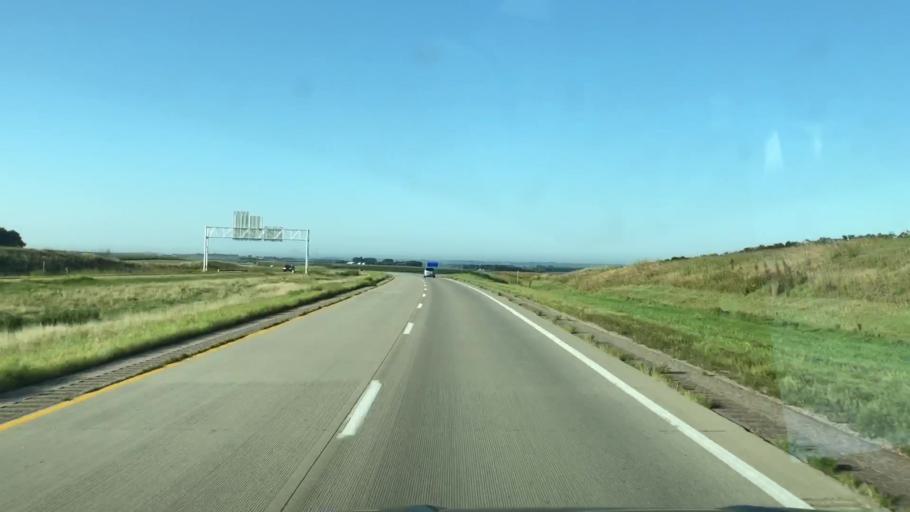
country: US
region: Iowa
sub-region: Plymouth County
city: Le Mars
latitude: 42.8104
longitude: -96.1961
